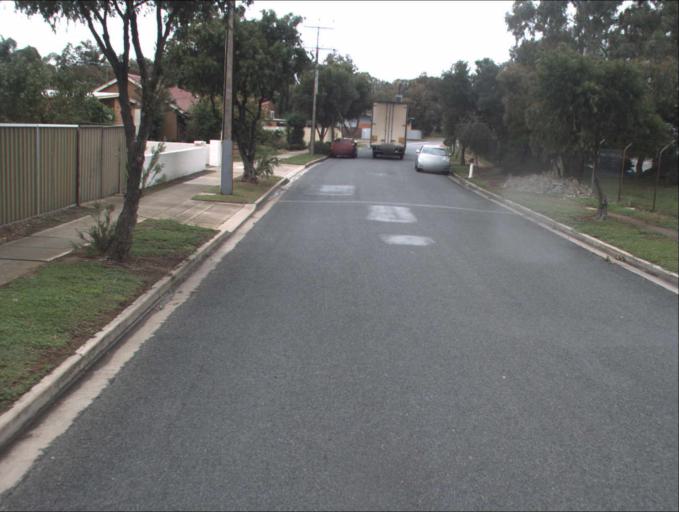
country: AU
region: South Australia
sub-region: Prospect
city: Prospect
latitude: -34.8770
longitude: 138.5800
